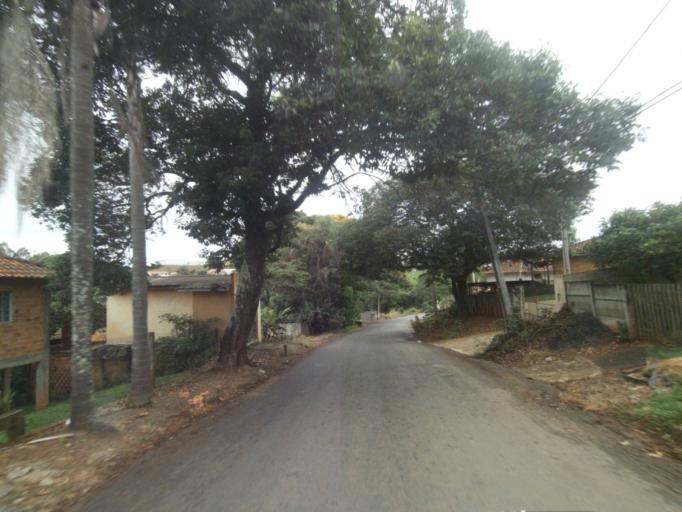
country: BR
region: Parana
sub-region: Telemaco Borba
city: Telemaco Borba
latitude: -24.3205
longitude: -50.6572
